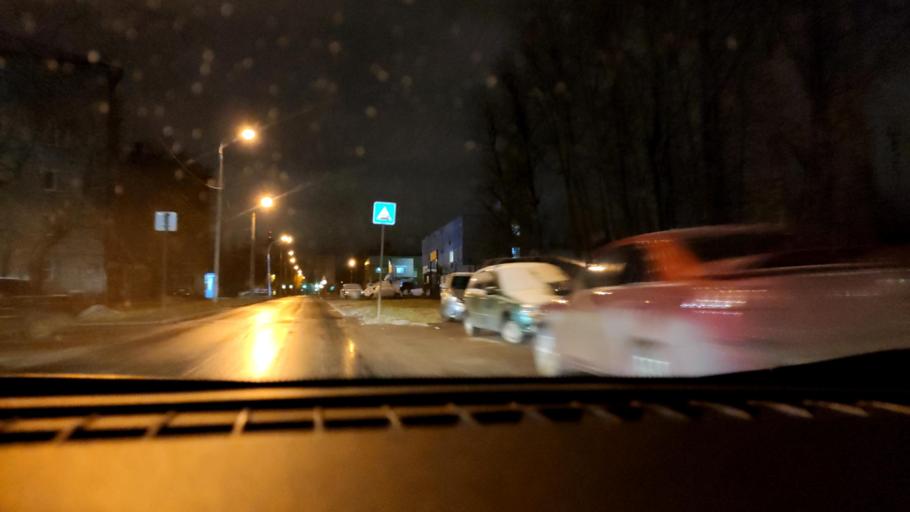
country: RU
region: Perm
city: Perm
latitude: 57.9835
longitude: 56.2092
